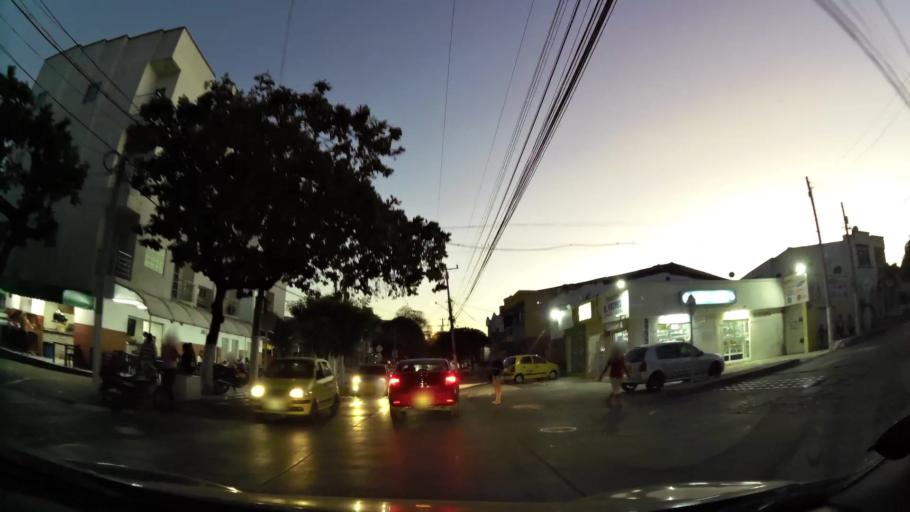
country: CO
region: Atlantico
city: Barranquilla
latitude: 10.9783
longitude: -74.8018
